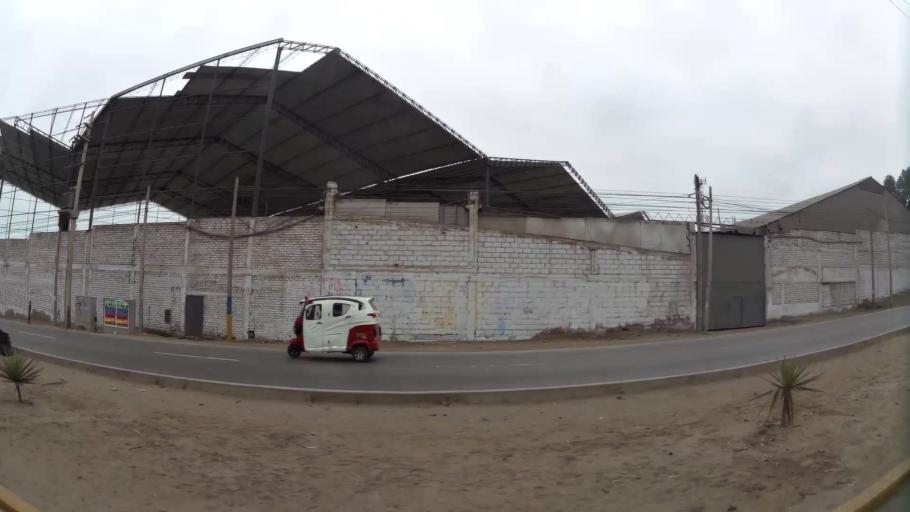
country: PE
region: Lima
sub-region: Lima
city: Surco
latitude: -12.2115
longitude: -76.9626
